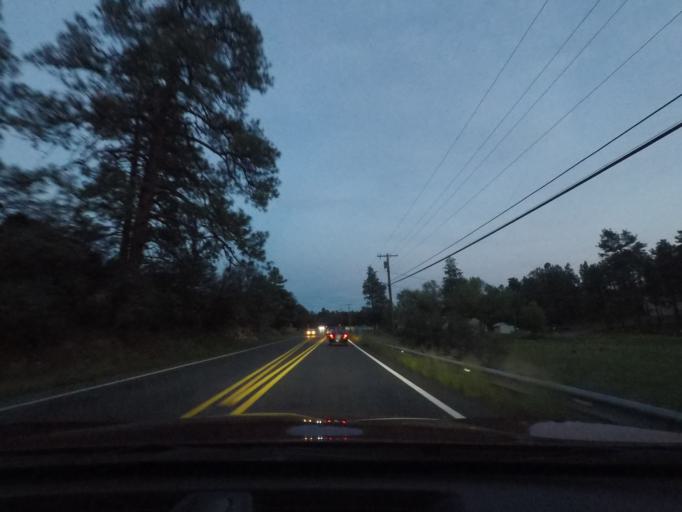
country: US
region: Arizona
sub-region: Yavapai County
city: Prescott
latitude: 34.5720
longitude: -112.5115
